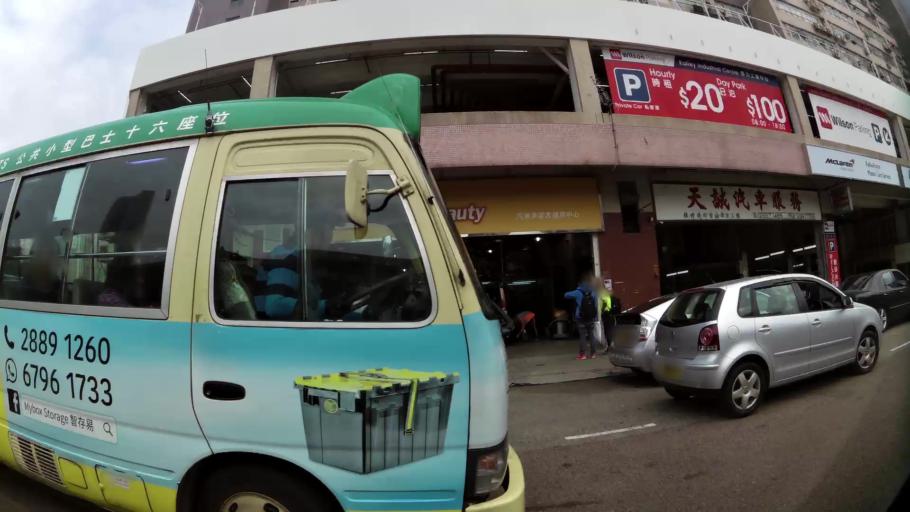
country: HK
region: Wanchai
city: Wan Chai
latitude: 22.2669
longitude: 114.2442
